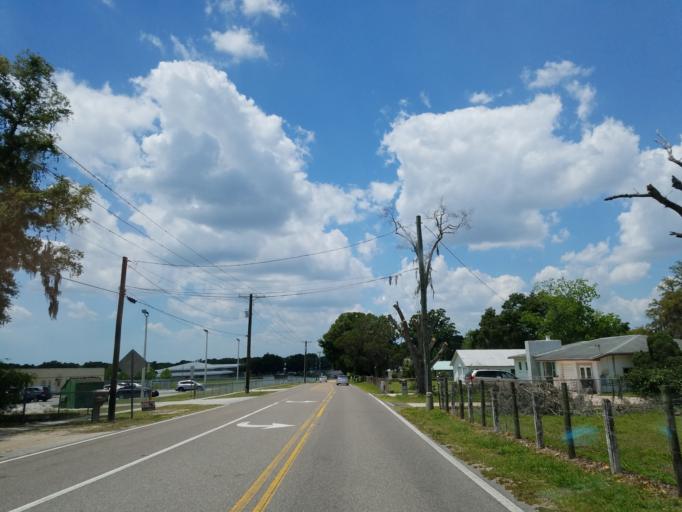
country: US
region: Florida
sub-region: Hillsborough County
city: Brandon
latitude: 27.9083
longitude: -82.2711
